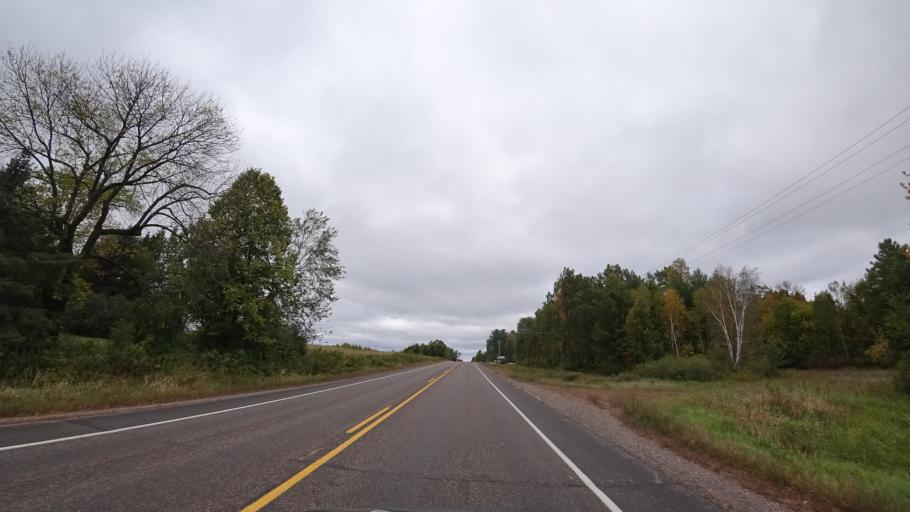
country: US
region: Wisconsin
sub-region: Rusk County
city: Ladysmith
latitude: 45.3681
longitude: -91.1106
